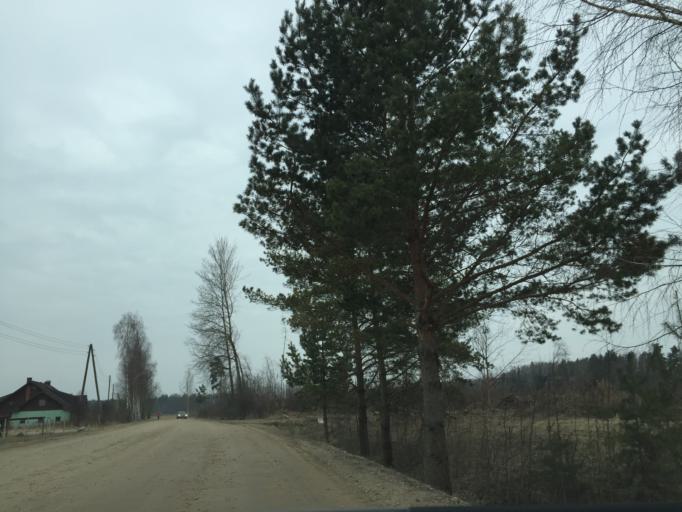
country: LV
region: Kekava
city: Kekava
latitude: 56.8043
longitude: 24.1679
